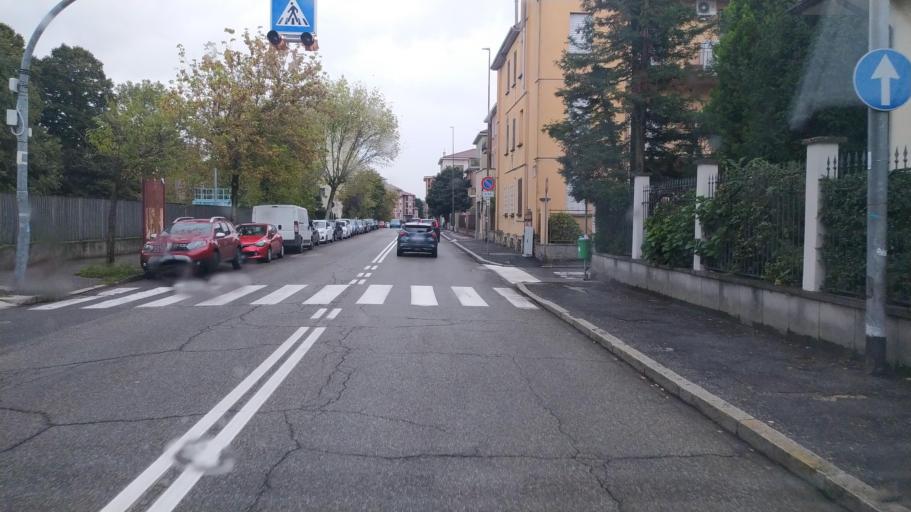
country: IT
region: Lombardy
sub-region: Provincia di Pavia
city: Pavia
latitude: 45.1949
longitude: 9.1639
